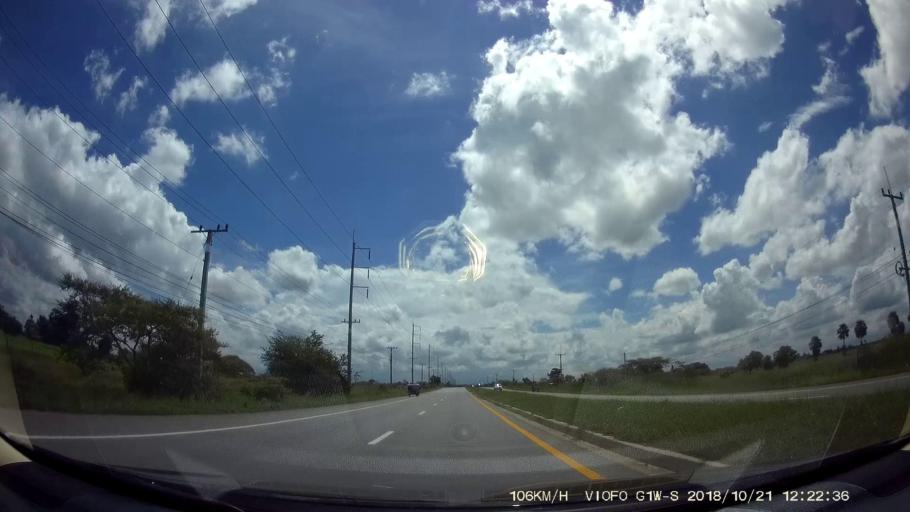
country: TH
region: Nakhon Ratchasima
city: Dan Khun Thot
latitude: 15.2586
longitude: 101.7894
